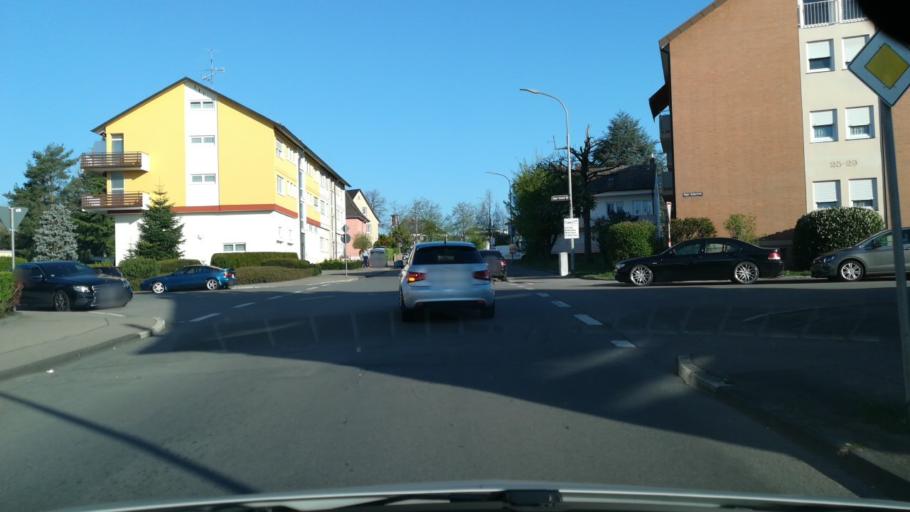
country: DE
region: Baden-Wuerttemberg
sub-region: Freiburg Region
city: Singen
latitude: 47.7657
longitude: 8.8427
